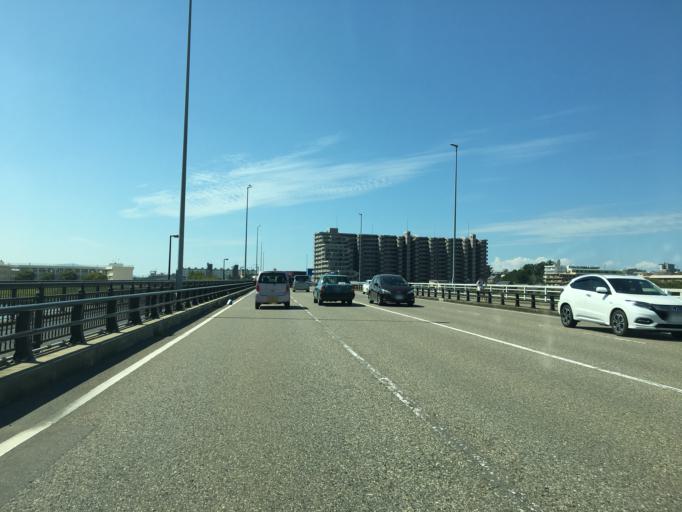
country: JP
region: Niigata
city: Niigata-shi
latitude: 37.8980
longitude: 139.0112
